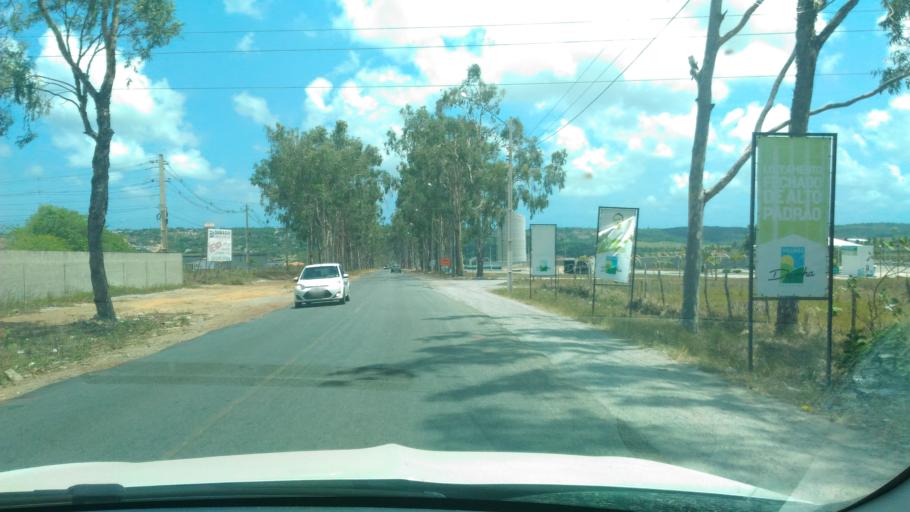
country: BR
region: Paraiba
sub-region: Conde
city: Conde
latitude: -7.2605
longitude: -34.9340
